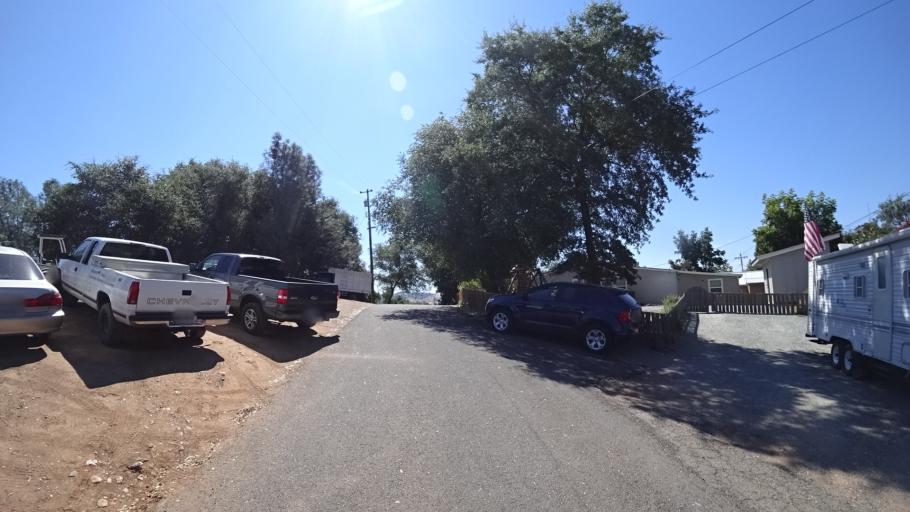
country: US
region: California
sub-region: Calaveras County
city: Angels Camp
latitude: 38.0752
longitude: -120.5494
